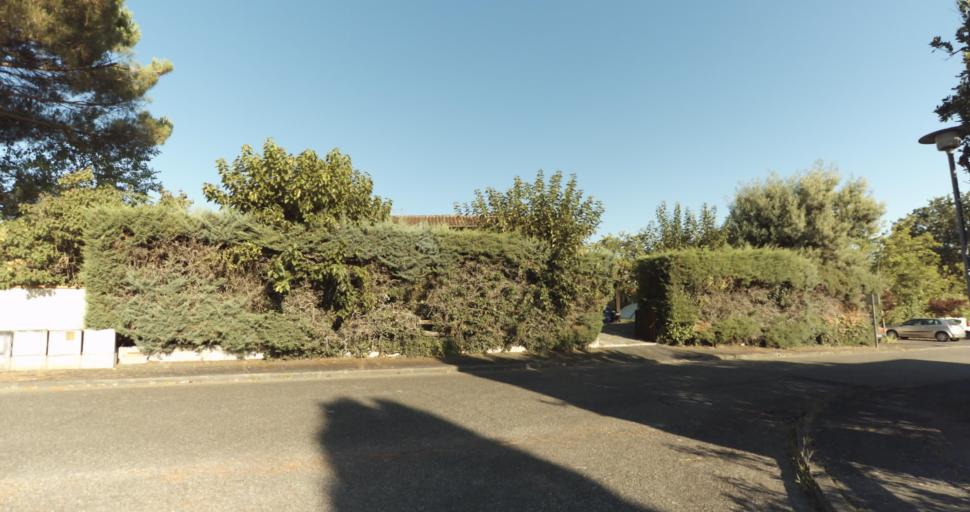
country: FR
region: Midi-Pyrenees
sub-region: Departement de la Haute-Garonne
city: Saint-Jean
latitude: 43.6537
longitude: 1.4968
